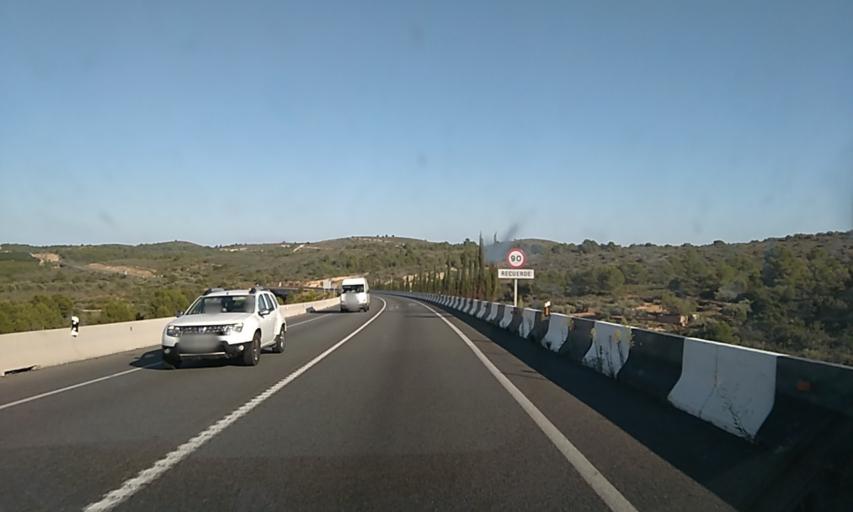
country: ES
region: Valencia
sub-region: Provincia de Castello
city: Torreblanca
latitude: 40.2102
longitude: 0.1355
